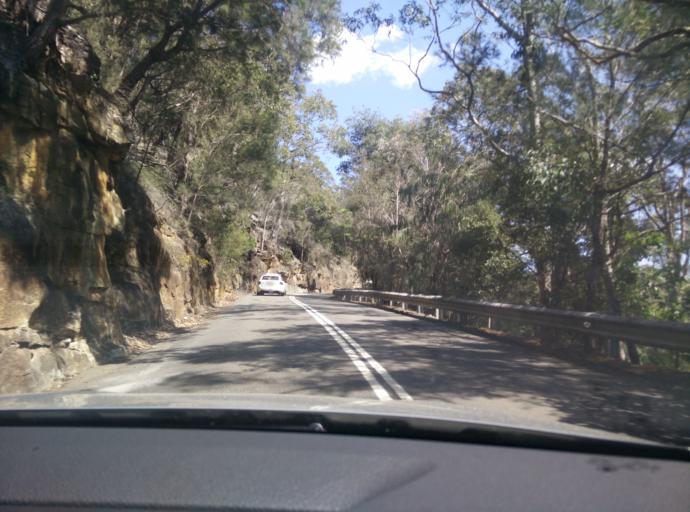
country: AU
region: New South Wales
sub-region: Gosford Shire
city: Umina
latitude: -33.5356
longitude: 151.3091
